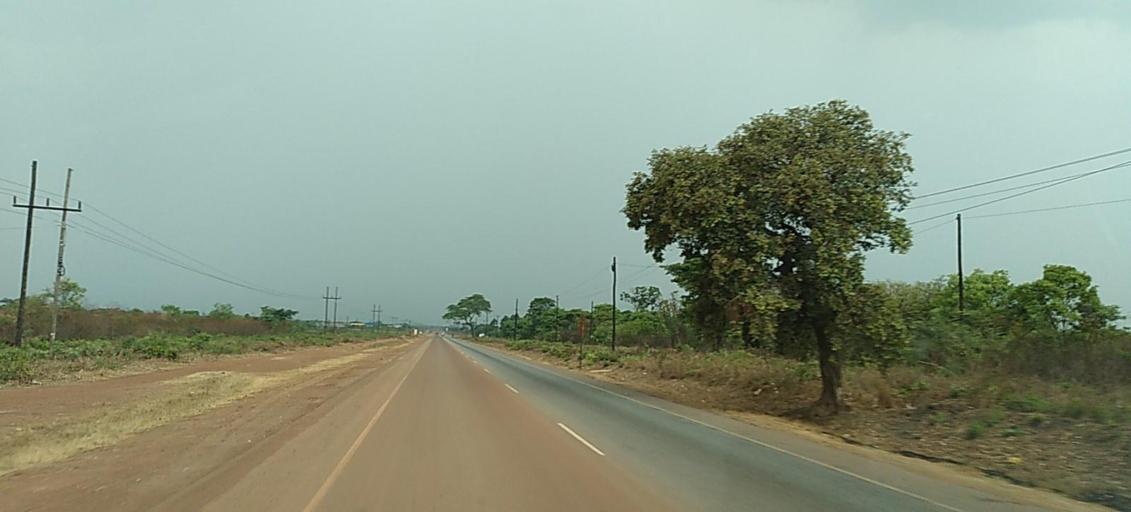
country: ZM
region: Copperbelt
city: Kalulushi
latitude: -12.8340
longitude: 28.1130
